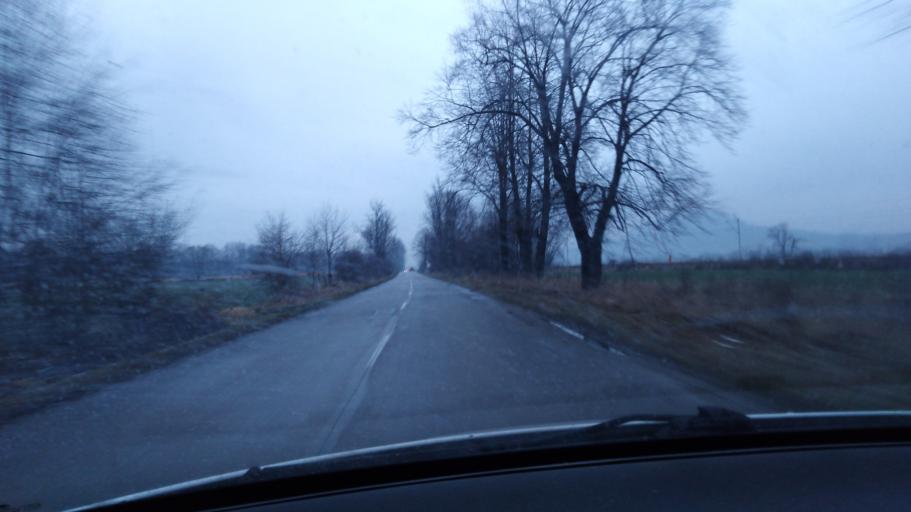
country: PL
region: Silesian Voivodeship
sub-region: Powiat zywiecki
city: Wieprz
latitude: 49.6374
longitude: 19.1563
